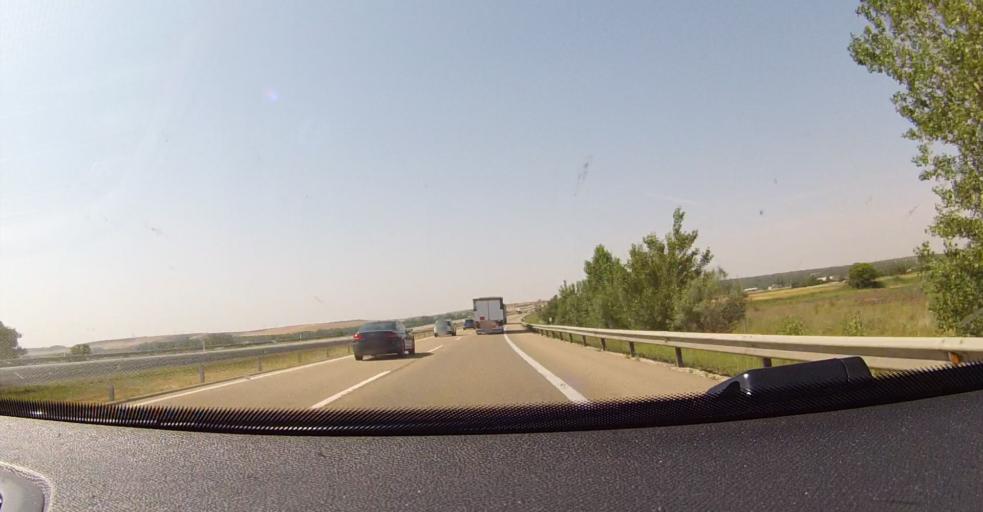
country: ES
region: Castille and Leon
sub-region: Provincia de Burgos
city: Cardenajimeno
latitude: 42.3466
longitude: -3.6044
